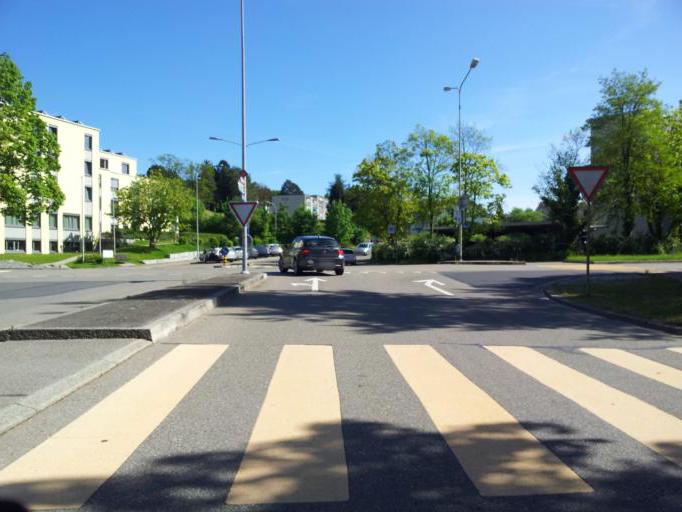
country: CH
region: Zurich
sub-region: Bezirk Dietikon
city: Schlieren / Spital
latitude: 47.3927
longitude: 8.4288
